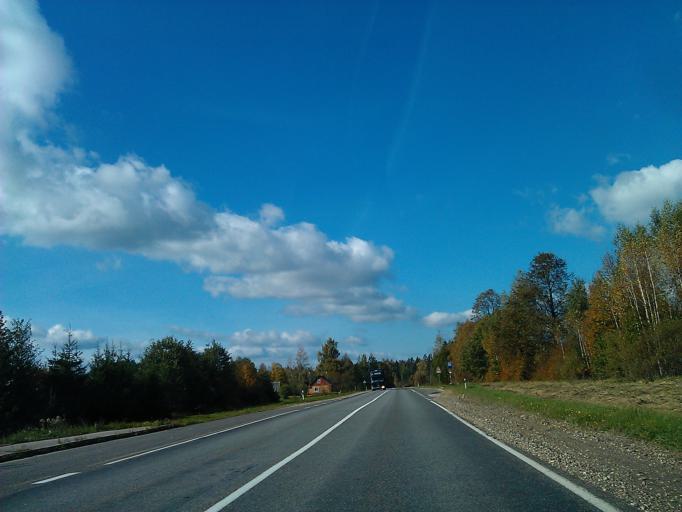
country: LV
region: Livani
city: Livani
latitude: 56.2244
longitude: 26.2197
